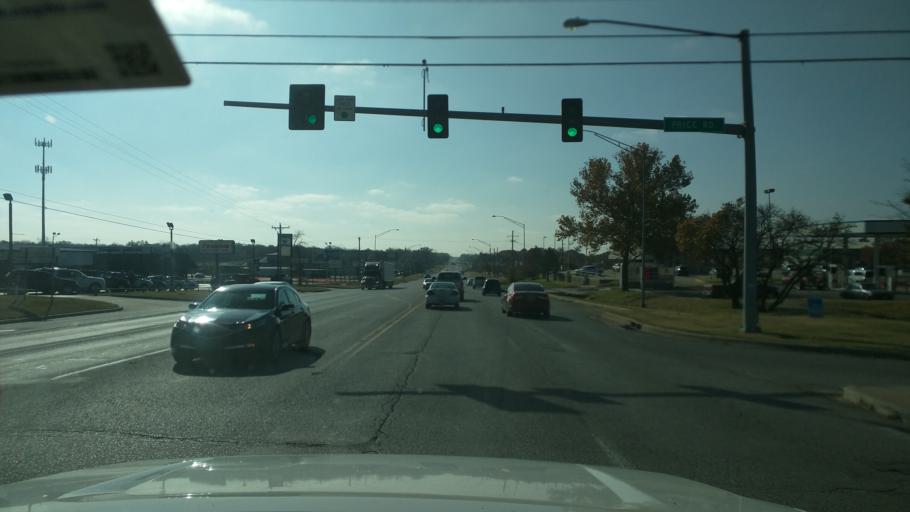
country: US
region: Oklahoma
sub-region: Washington County
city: Bartlesville
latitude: 36.7136
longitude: -95.9352
